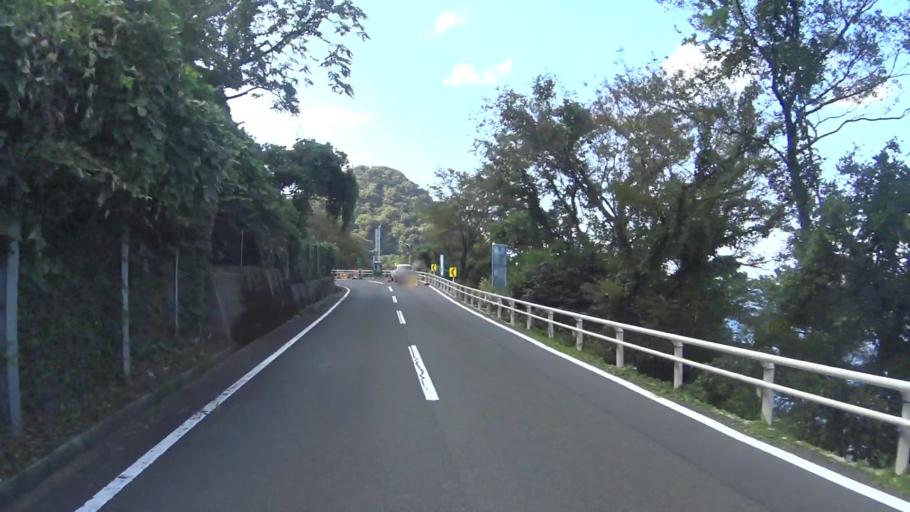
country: JP
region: Kyoto
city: Miyazu
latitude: 35.7674
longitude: 135.2338
